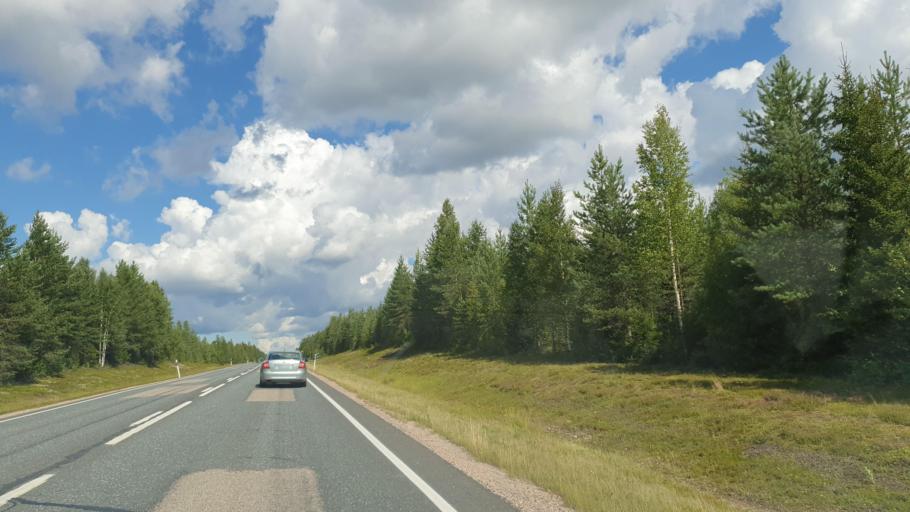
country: FI
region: Kainuu
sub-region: Kajaani
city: Kajaani
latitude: 64.0348
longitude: 27.4475
